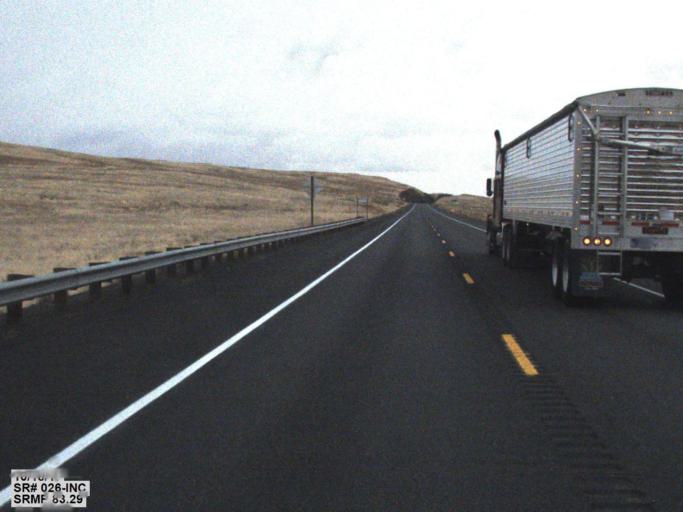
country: US
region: Washington
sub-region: Adams County
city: Ritzville
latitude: 46.7577
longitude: -118.3023
